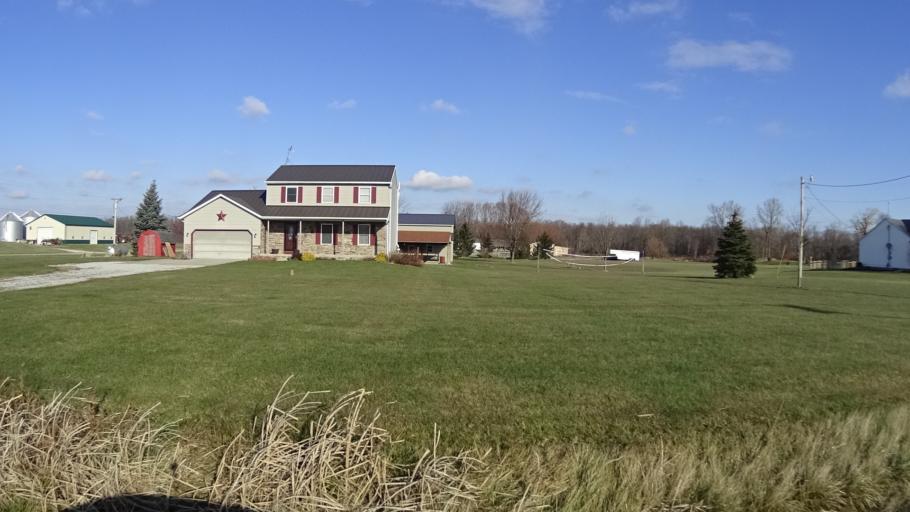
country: US
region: Ohio
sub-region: Lorain County
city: Wellington
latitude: 41.2235
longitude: -82.2358
